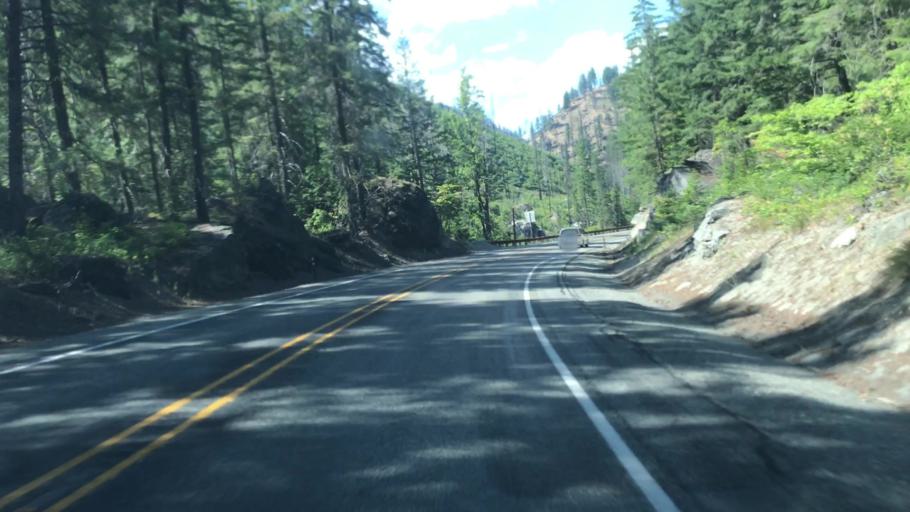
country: US
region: Washington
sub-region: Chelan County
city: Leavenworth
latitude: 47.6552
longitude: -120.7295
